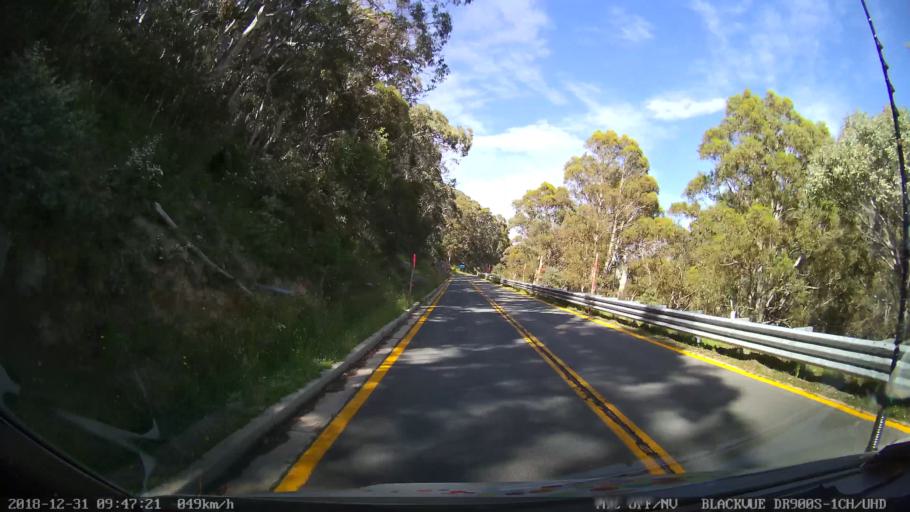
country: AU
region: New South Wales
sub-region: Snowy River
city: Jindabyne
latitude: -36.5080
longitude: 148.3024
